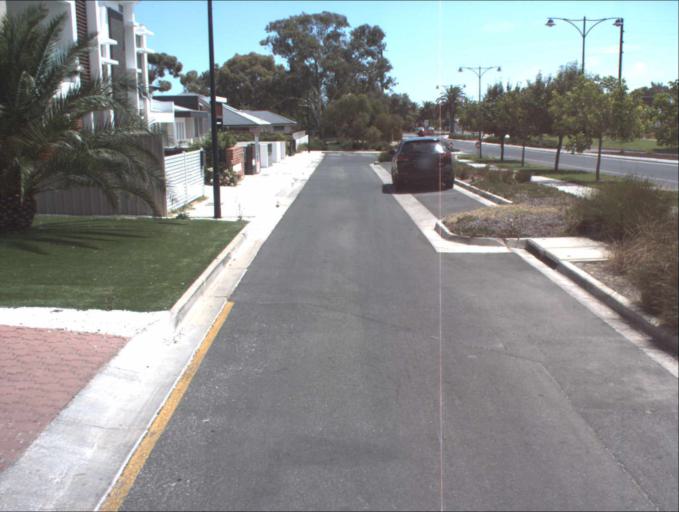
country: AU
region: South Australia
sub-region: Port Adelaide Enfield
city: Klemzig
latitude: -34.8583
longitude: 138.6288
